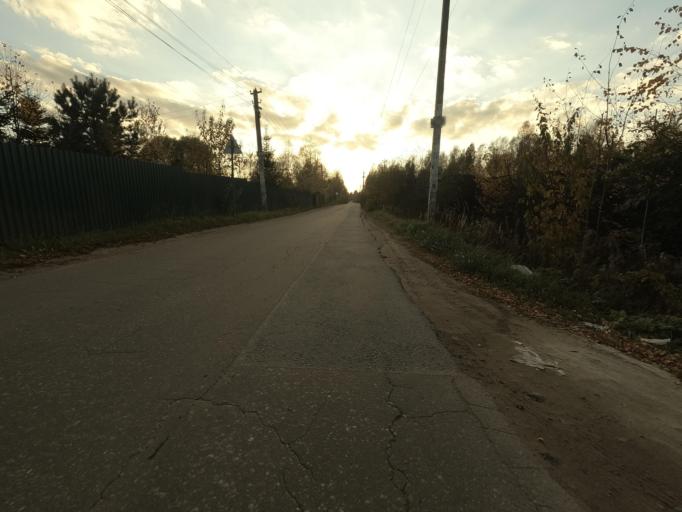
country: RU
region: St.-Petersburg
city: Beloostrov
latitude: 60.1873
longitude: 30.0656
